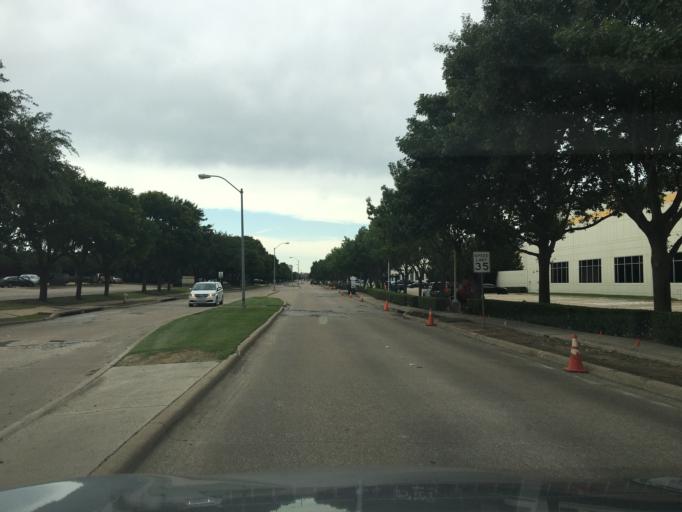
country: US
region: Texas
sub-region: Dallas County
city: Richardson
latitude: 32.9684
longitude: -96.7064
